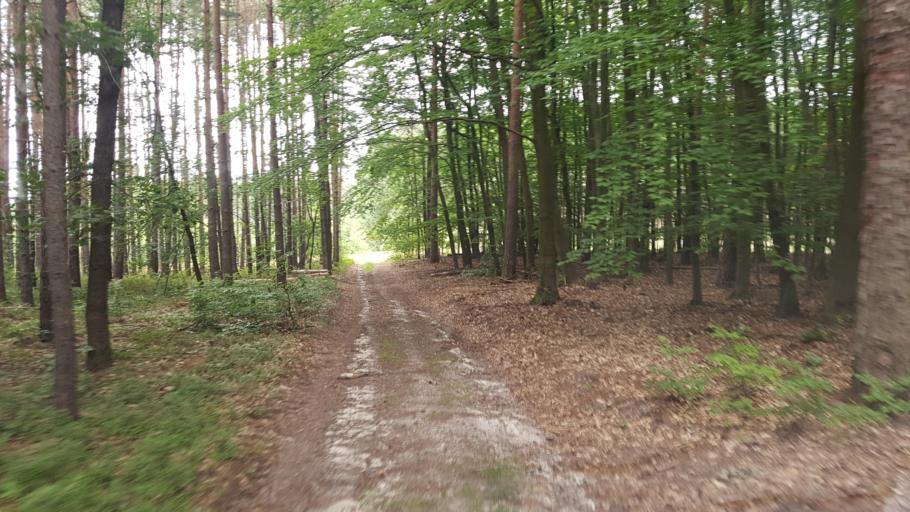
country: DE
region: Brandenburg
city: Crinitz
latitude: 51.7332
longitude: 13.7423
